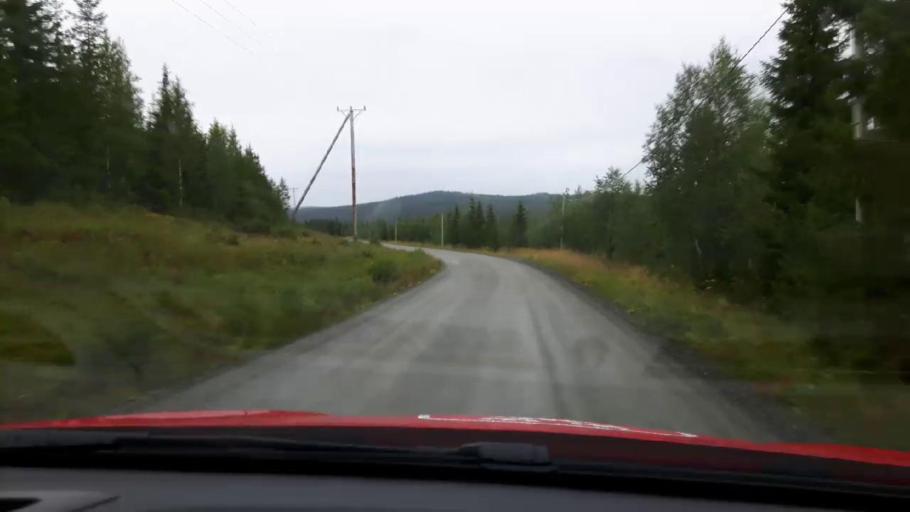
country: SE
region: Jaemtland
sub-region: Are Kommun
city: Are
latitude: 63.4149
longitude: 12.8265
